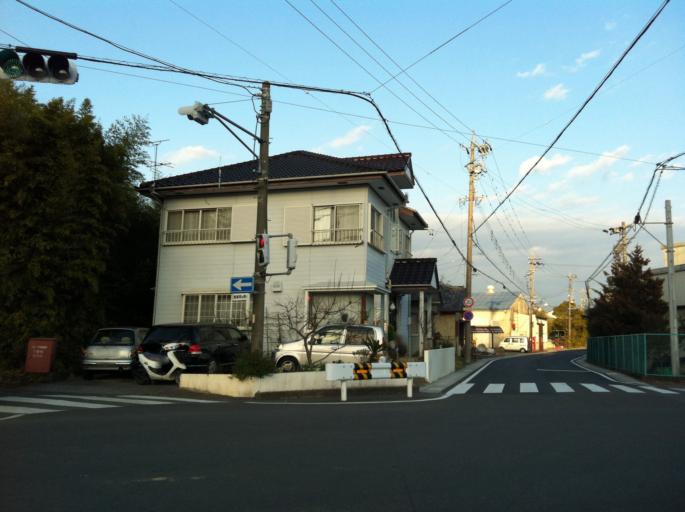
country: JP
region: Shizuoka
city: Shizuoka-shi
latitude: 35.0479
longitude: 138.4727
